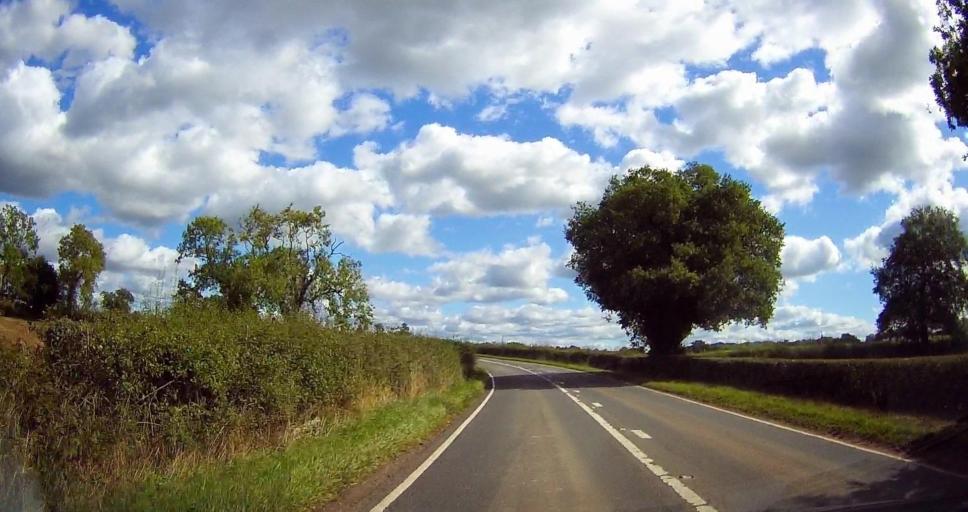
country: GB
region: England
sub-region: Cheshire East
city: Chorlton
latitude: 52.9835
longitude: -2.4473
